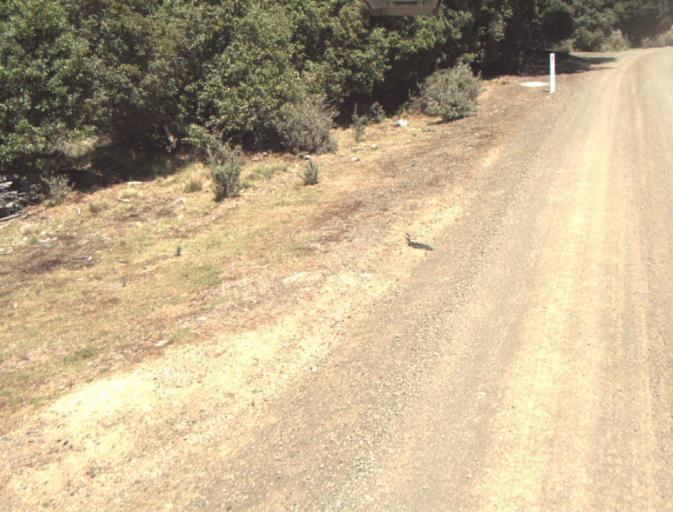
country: AU
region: Tasmania
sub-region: Dorset
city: Scottsdale
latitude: -41.3649
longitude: 147.4311
